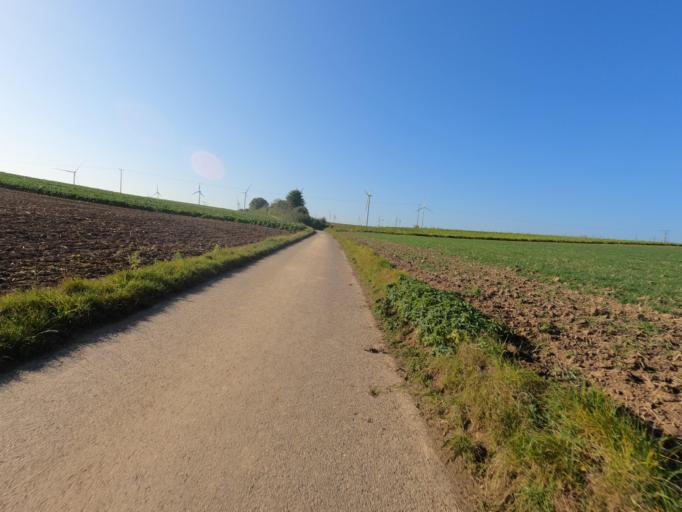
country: DE
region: North Rhine-Westphalia
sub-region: Regierungsbezirk Koln
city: Linnich
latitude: 50.9975
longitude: 6.2423
